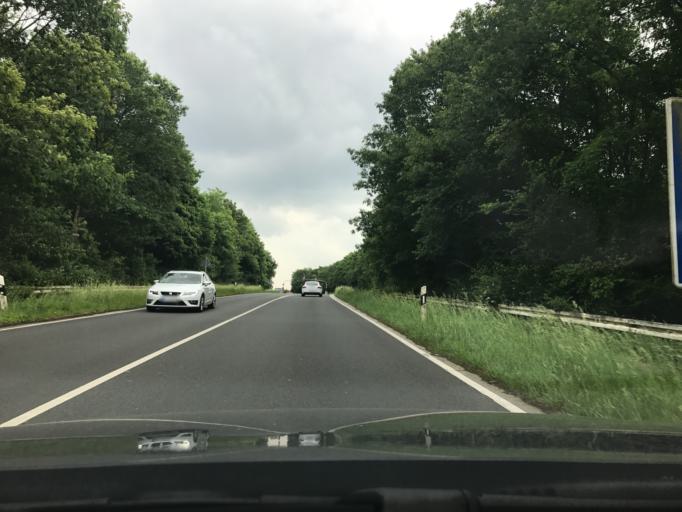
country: DE
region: North Rhine-Westphalia
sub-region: Regierungsbezirk Dusseldorf
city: Ratingen
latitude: 51.3007
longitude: 6.8028
